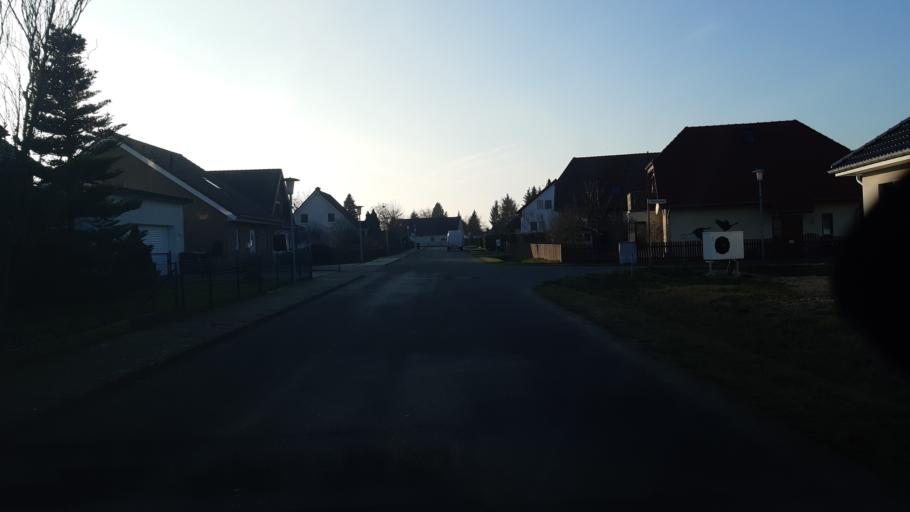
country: DE
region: Brandenburg
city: Velten
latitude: 52.7150
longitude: 13.1501
